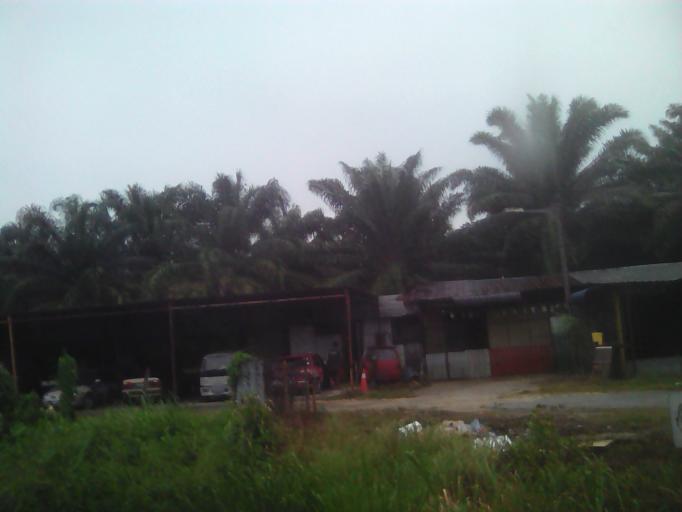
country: MY
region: Kedah
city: Kulim
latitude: 5.3946
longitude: 100.5469
